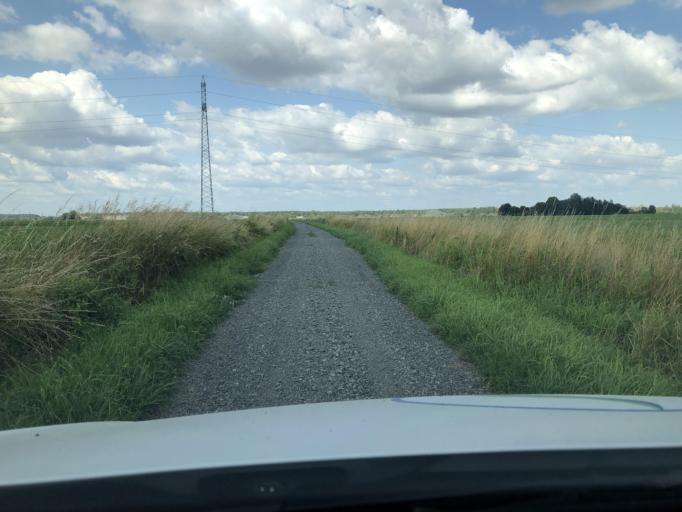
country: SE
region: Skane
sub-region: Kristianstads Kommun
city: Degeberga
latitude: 55.8841
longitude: 14.0818
